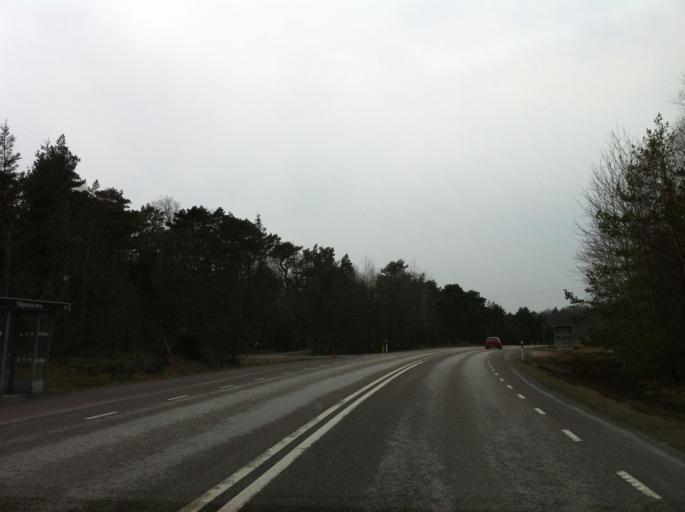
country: SE
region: Vaestra Goetaland
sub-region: Orust
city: Henan
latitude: 58.2942
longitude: 11.7030
